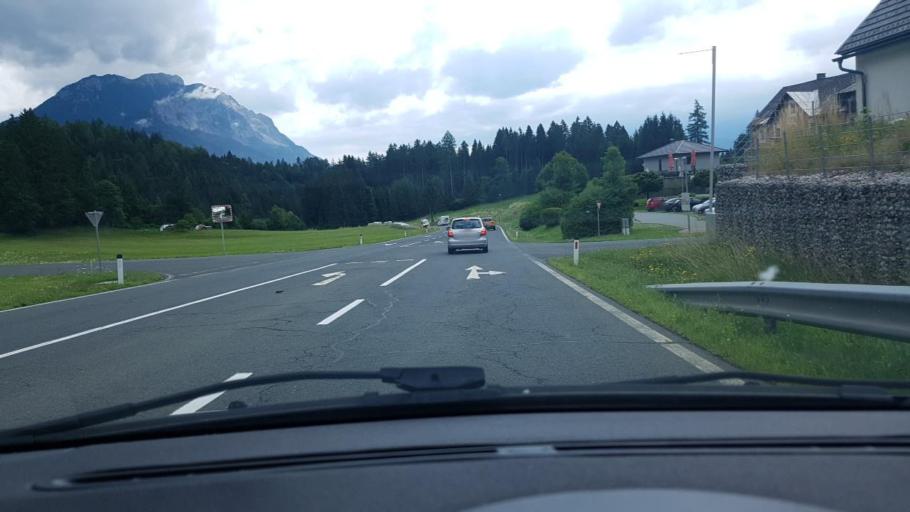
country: AT
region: Carinthia
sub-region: Politischer Bezirk Villach Land
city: Feistritz an der Gail
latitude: 46.6054
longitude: 13.5557
